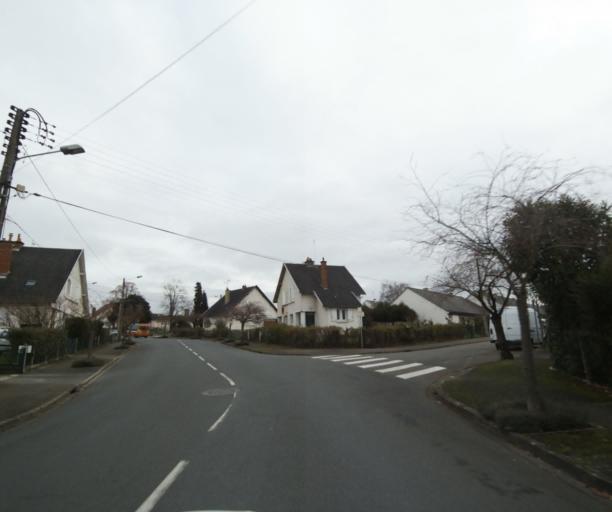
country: FR
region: Pays de la Loire
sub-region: Departement de la Sarthe
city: Le Mans
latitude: 47.9729
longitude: 0.2005
